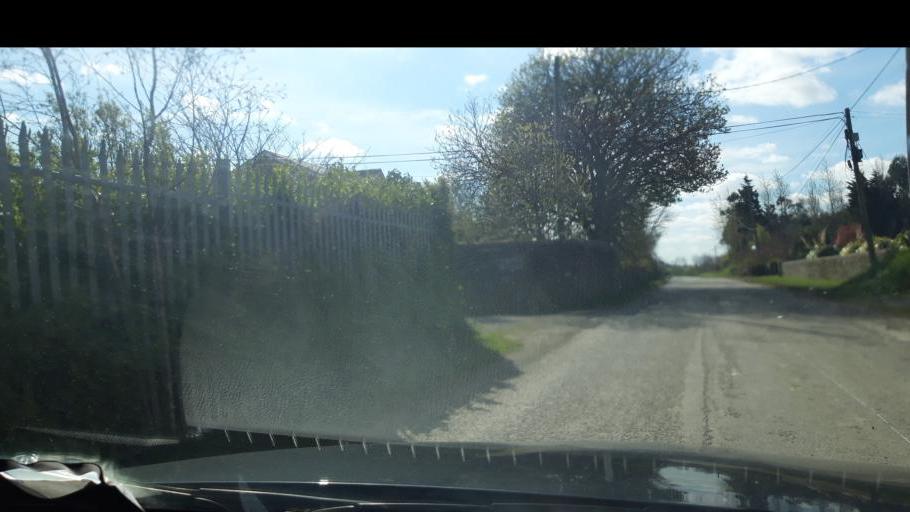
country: IE
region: Leinster
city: Malahide
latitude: 53.4294
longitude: -6.1682
